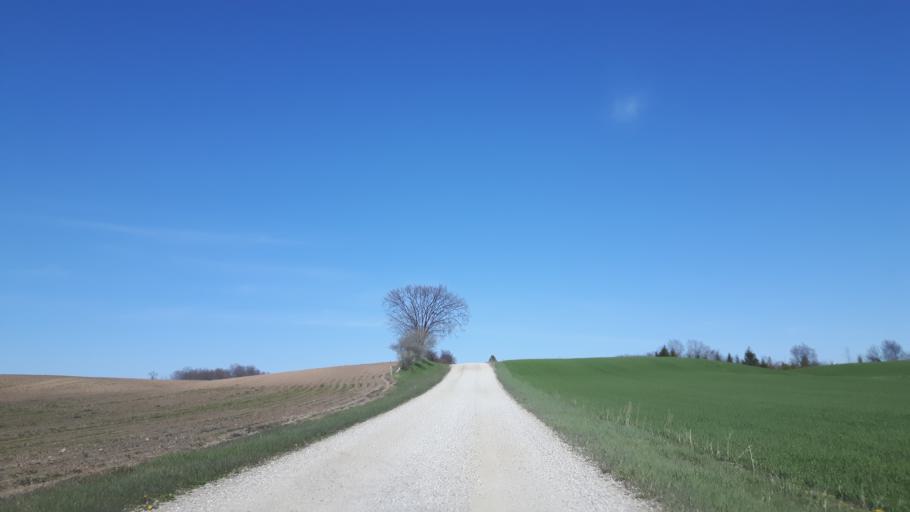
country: CA
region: Ontario
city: Goderich
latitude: 43.6613
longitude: -81.6820
